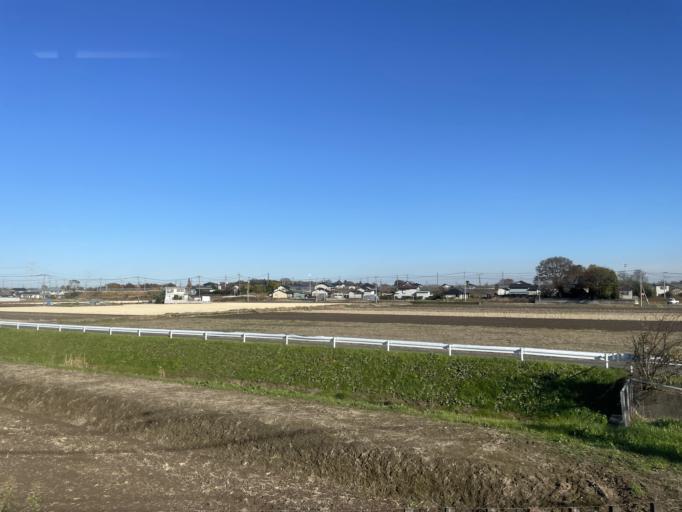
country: JP
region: Saitama
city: Satte
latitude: 36.1058
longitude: 139.7204
